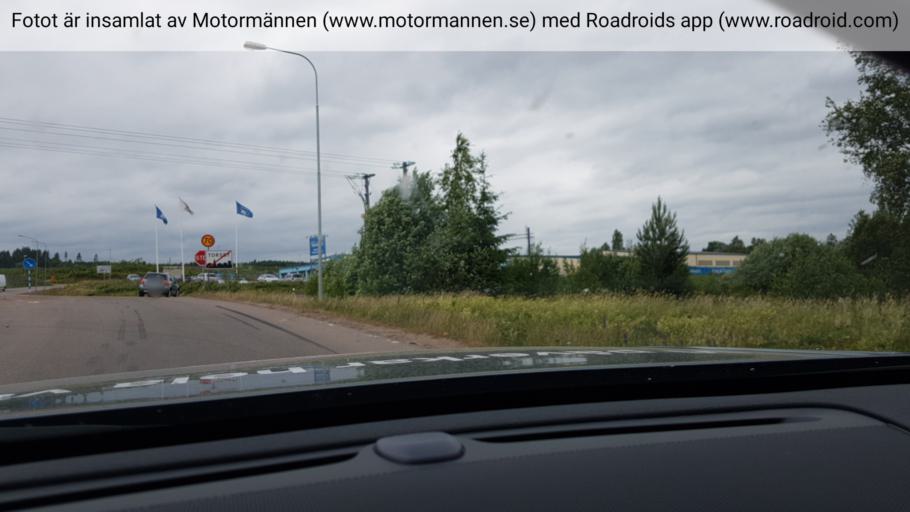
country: SE
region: Vaermland
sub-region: Torsby Kommun
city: Torsby
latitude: 60.1504
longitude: 13.0027
